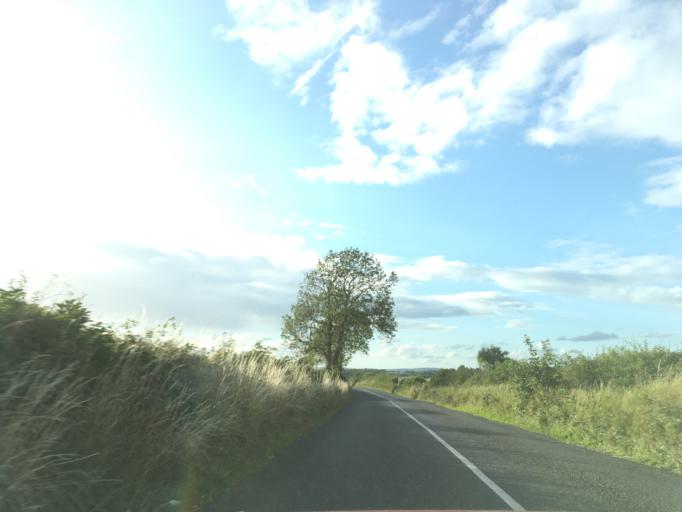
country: IE
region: Munster
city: Cashel
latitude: 52.4756
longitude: -7.9257
